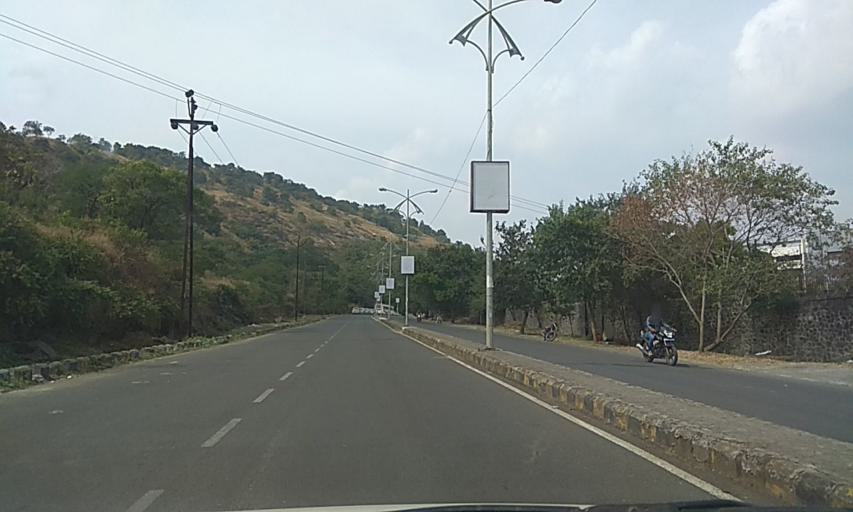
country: IN
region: Maharashtra
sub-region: Pune Division
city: Pimpri
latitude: 18.5994
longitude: 73.7166
